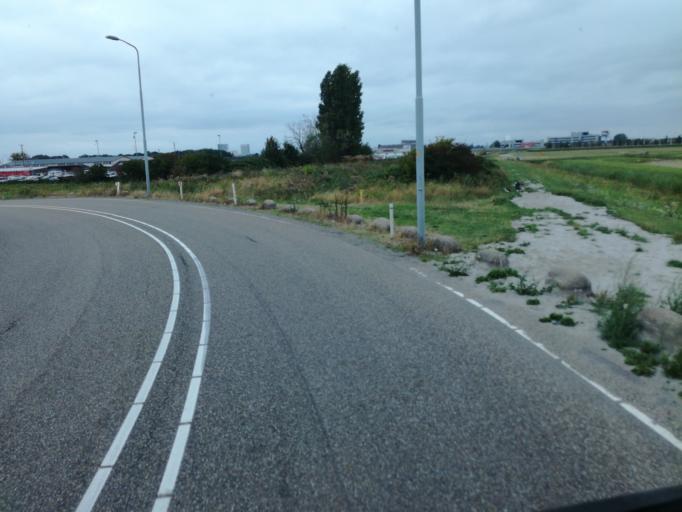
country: NL
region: North Holland
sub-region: Gemeente Aalsmeer
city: Aalsmeer
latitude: 52.2851
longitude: 4.7359
